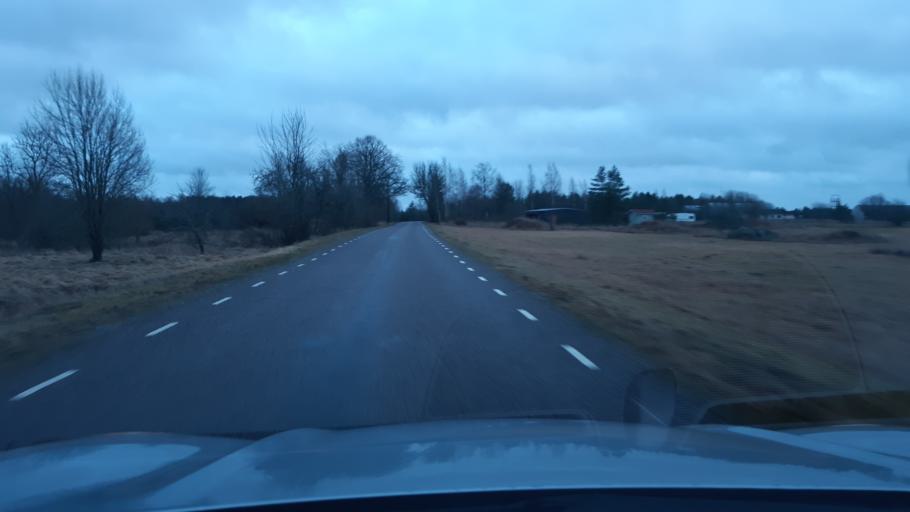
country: EE
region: Raplamaa
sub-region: Rapla vald
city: Rapla
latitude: 58.9886
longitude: 24.7280
